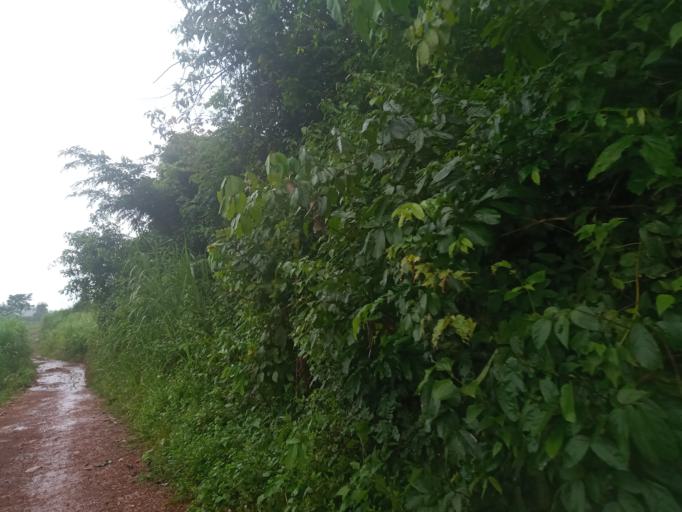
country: SL
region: Northern Province
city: Bumbuna
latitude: 8.9215
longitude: -11.7426
